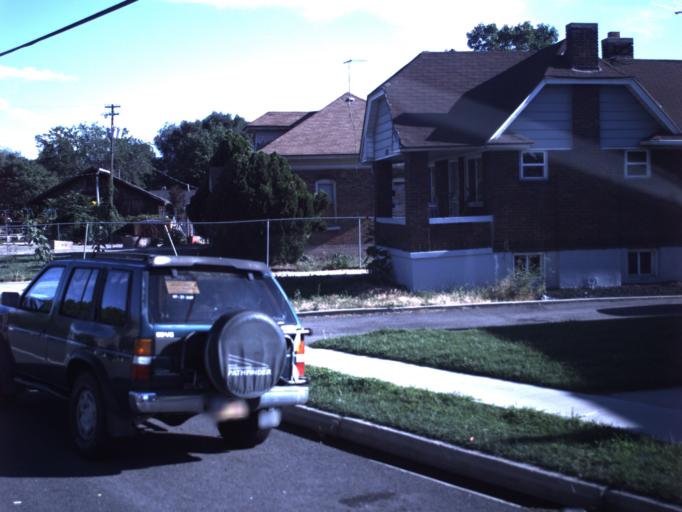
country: US
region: Utah
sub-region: Utah County
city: Provo
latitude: 40.2282
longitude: -111.6454
